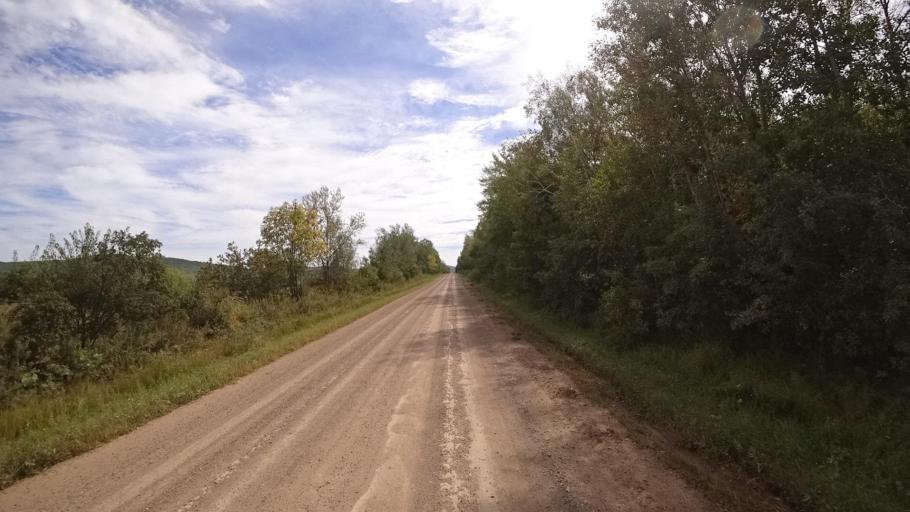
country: RU
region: Primorskiy
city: Yakovlevka
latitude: 44.6115
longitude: 133.5995
